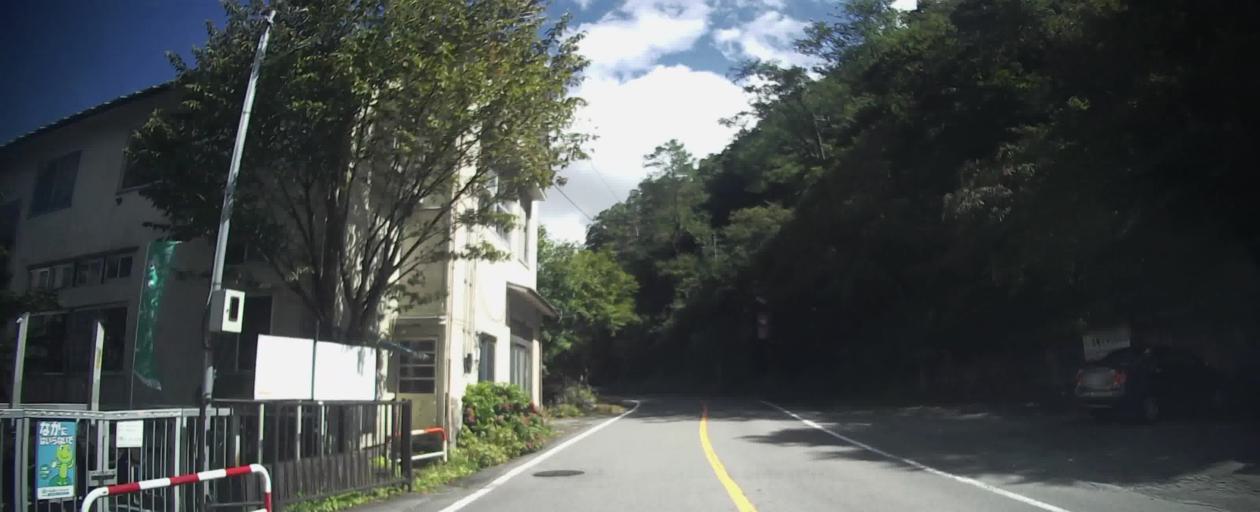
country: JP
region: Gunma
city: Nakanojomachi
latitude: 36.4703
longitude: 138.8624
